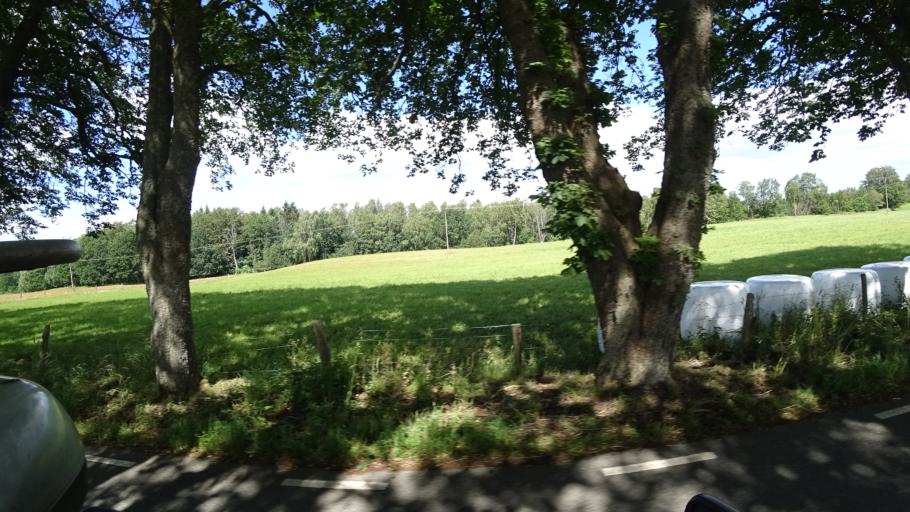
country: SE
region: Skane
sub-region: Kristianstads Kommun
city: Degeberga
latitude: 55.7127
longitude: 13.9768
